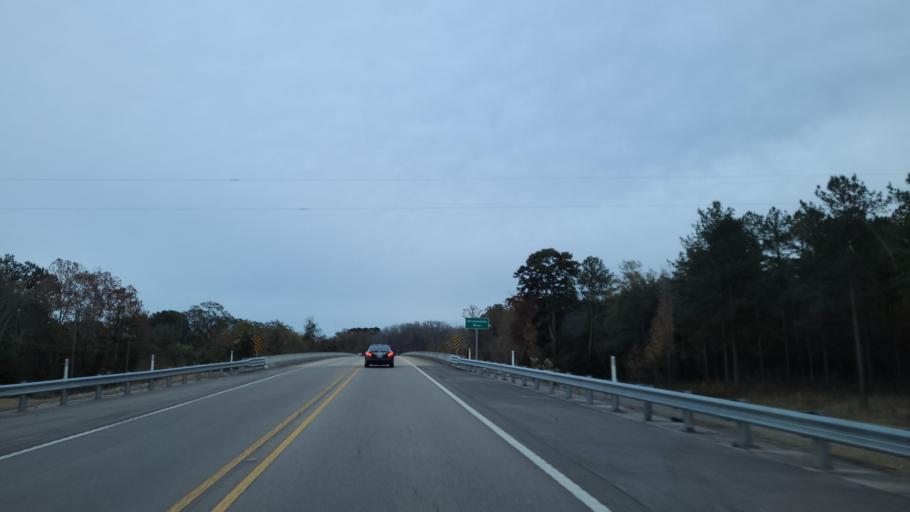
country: US
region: Mississippi
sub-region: Clarke County
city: Quitman
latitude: 32.0425
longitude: -88.7460
